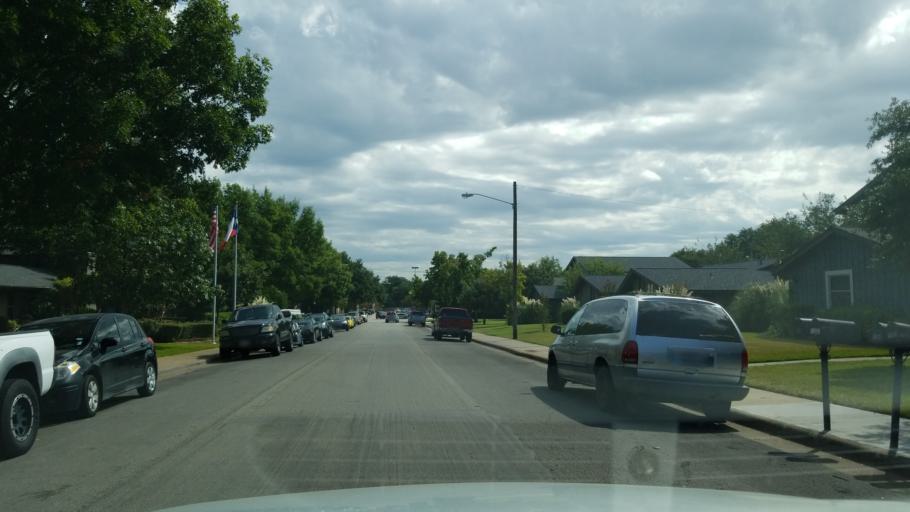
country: US
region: Texas
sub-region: Dallas County
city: Richardson
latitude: 32.9605
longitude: -96.7705
